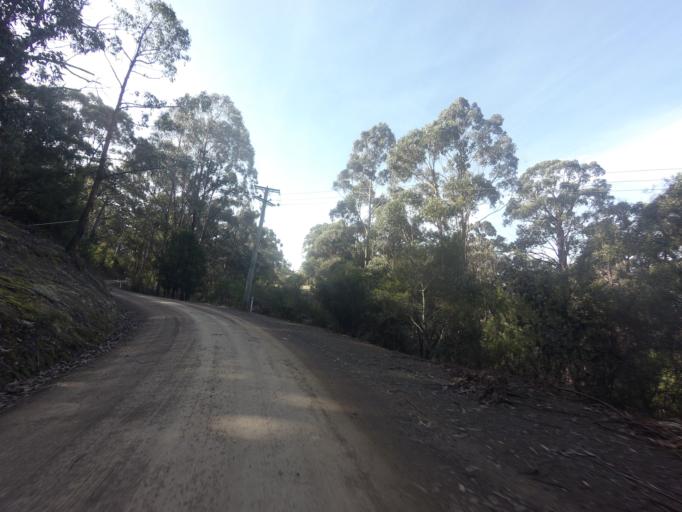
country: AU
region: Tasmania
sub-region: Kingborough
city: Kettering
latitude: -43.1022
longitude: 147.2601
